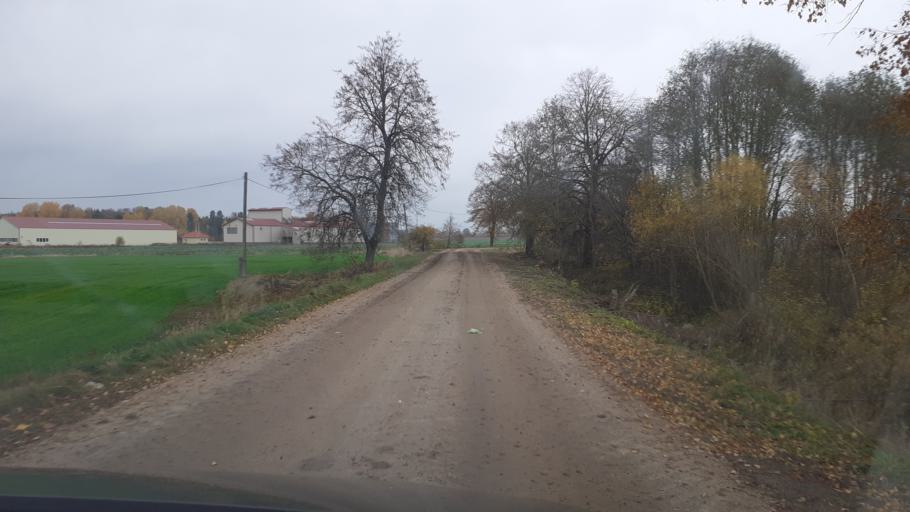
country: LV
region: Skrunda
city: Skrunda
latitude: 56.8515
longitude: 22.2143
